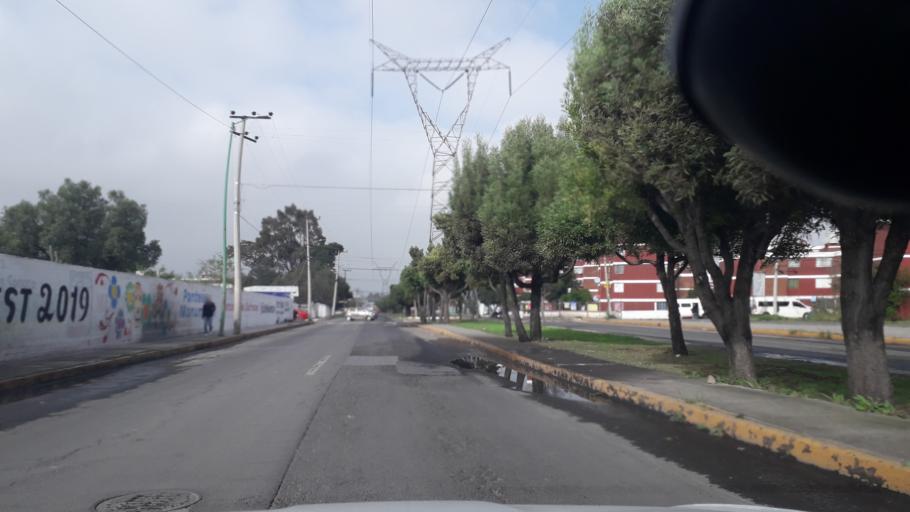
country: MX
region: Mexico
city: Coacalco
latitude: 19.6446
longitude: -99.0824
